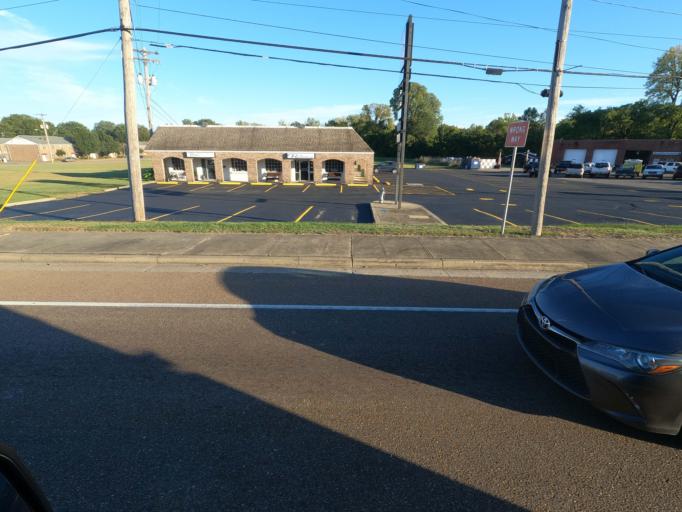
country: US
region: Tennessee
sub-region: Shelby County
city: Millington
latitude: 35.3357
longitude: -89.9161
